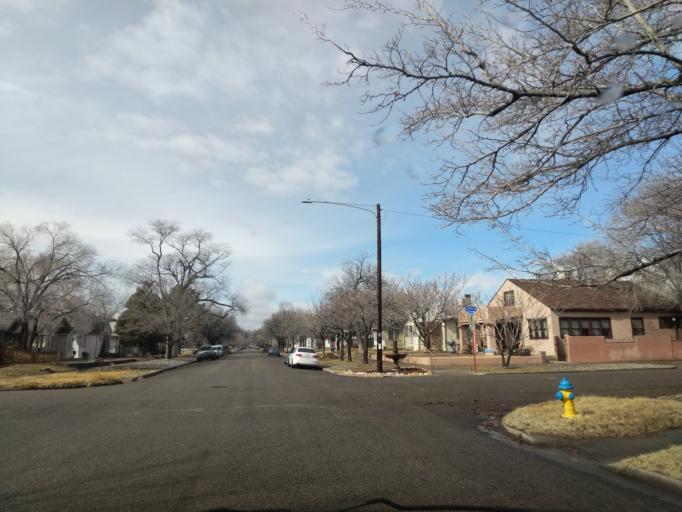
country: US
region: Colorado
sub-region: Mesa County
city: Grand Junction
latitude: 39.0755
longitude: -108.5573
